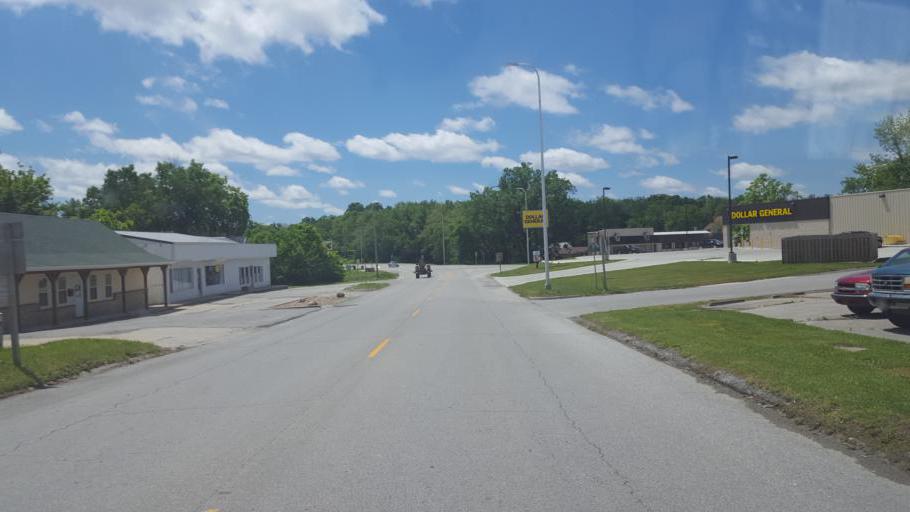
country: US
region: Missouri
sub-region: Harrison County
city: Bethany
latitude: 40.2697
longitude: -94.0273
